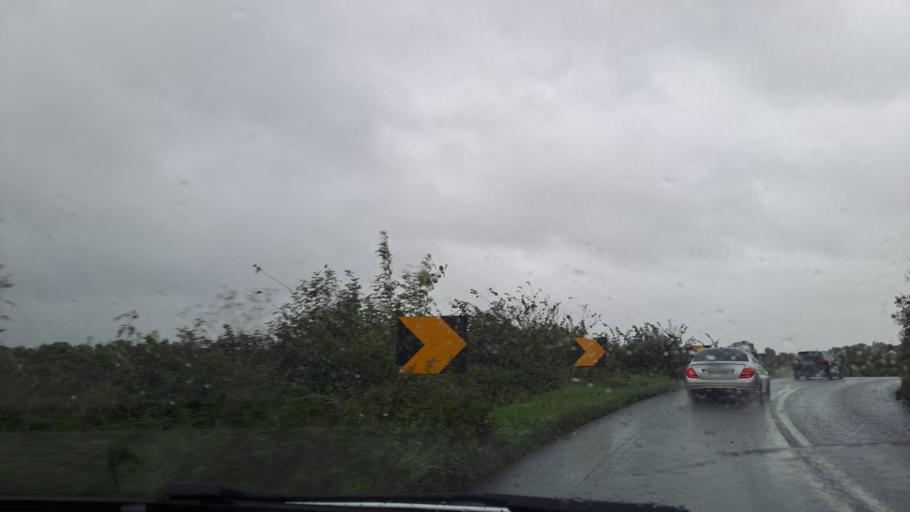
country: IE
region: Ulster
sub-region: County Monaghan
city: Carrickmacross
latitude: 53.9755
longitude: -6.6383
